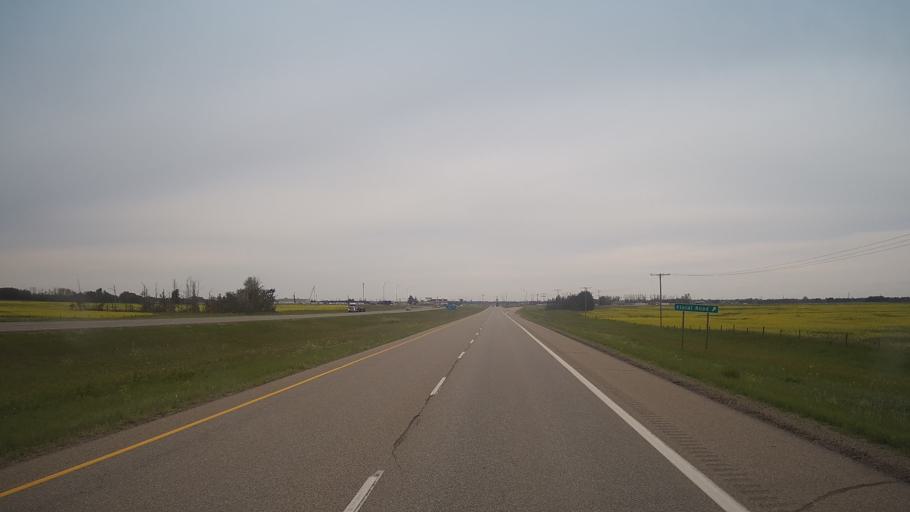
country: CA
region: Saskatchewan
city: Saskatoon
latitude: 52.0449
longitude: -106.5919
